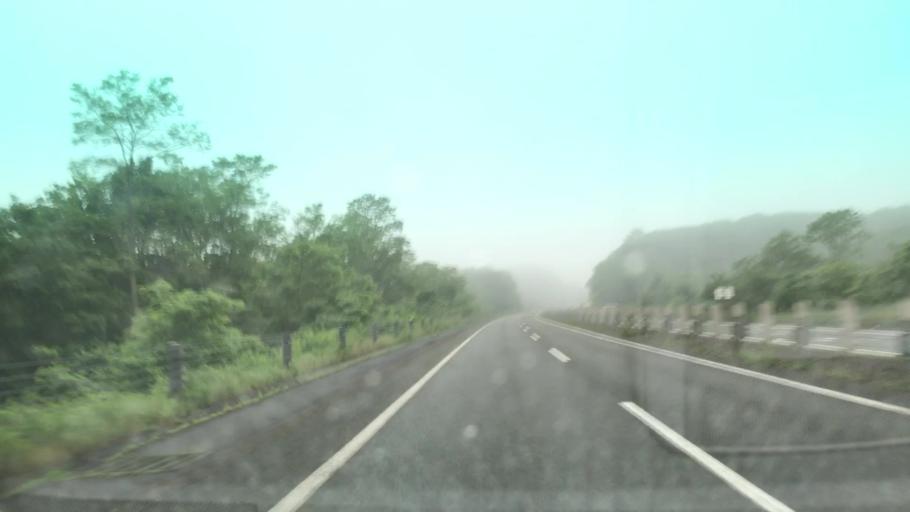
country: JP
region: Hokkaido
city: Tomakomai
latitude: 42.6438
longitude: 141.5267
